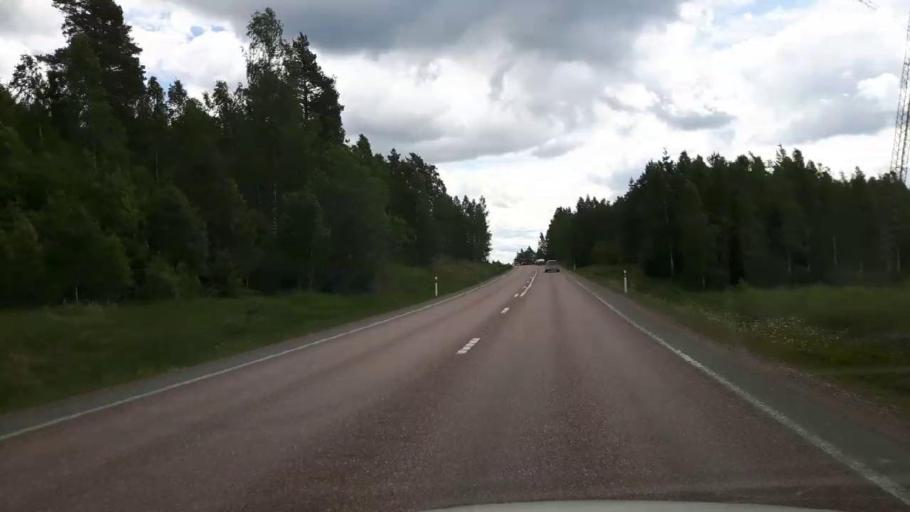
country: SE
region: Dalarna
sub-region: Saters Kommun
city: Saeter
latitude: 60.4864
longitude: 15.7685
